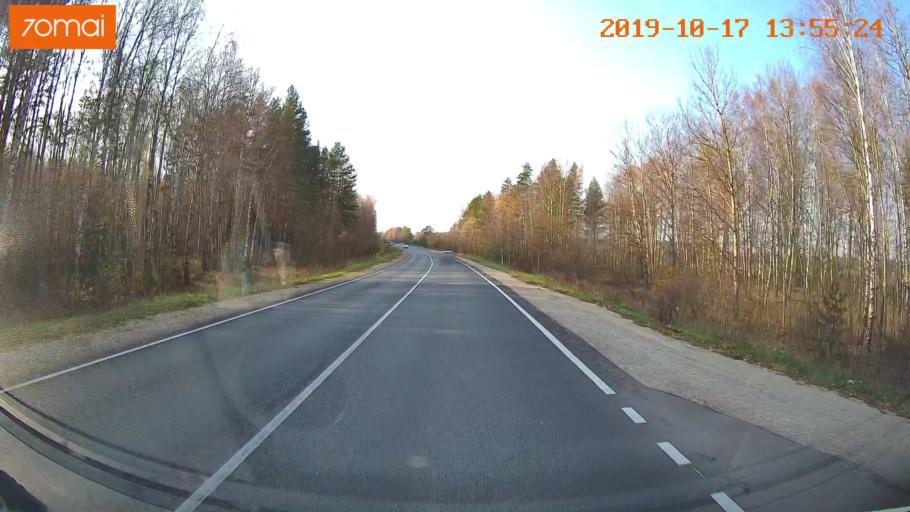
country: RU
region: Rjazan
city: Spas-Klepiki
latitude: 55.1520
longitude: 40.2904
